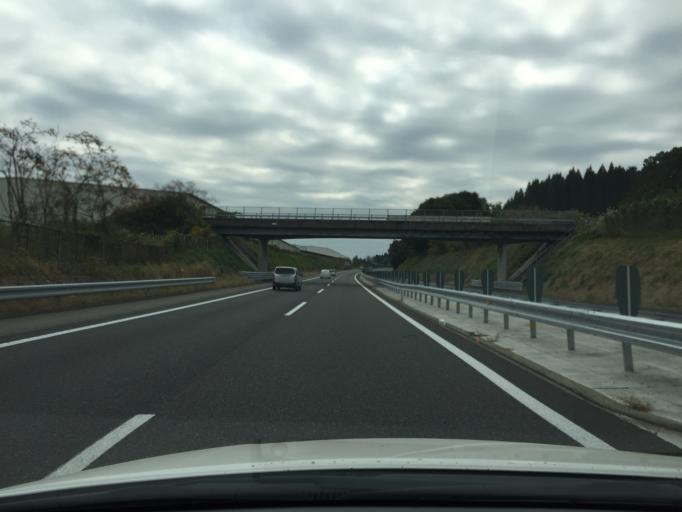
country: JP
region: Fukushima
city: Sukagawa
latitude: 37.2110
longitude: 140.3083
